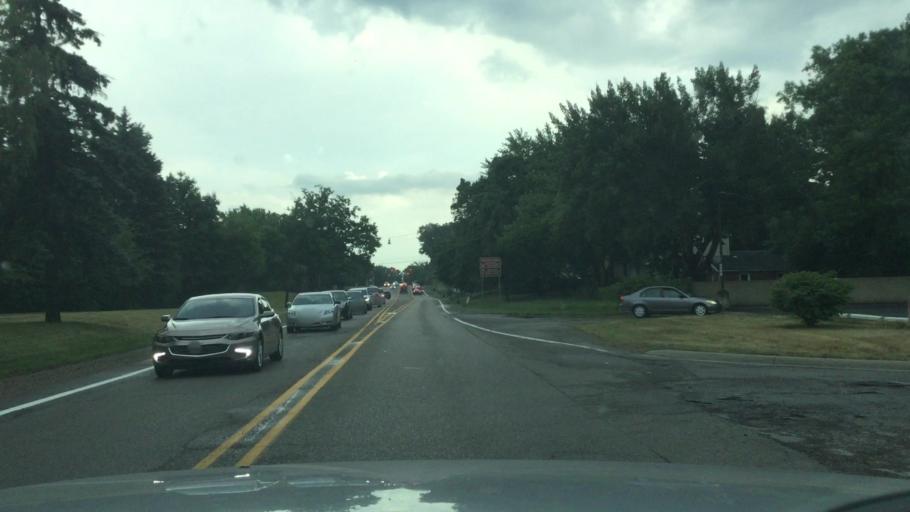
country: US
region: Michigan
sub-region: Oakland County
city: Sylvan Lake
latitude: 42.6654
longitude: -83.3470
